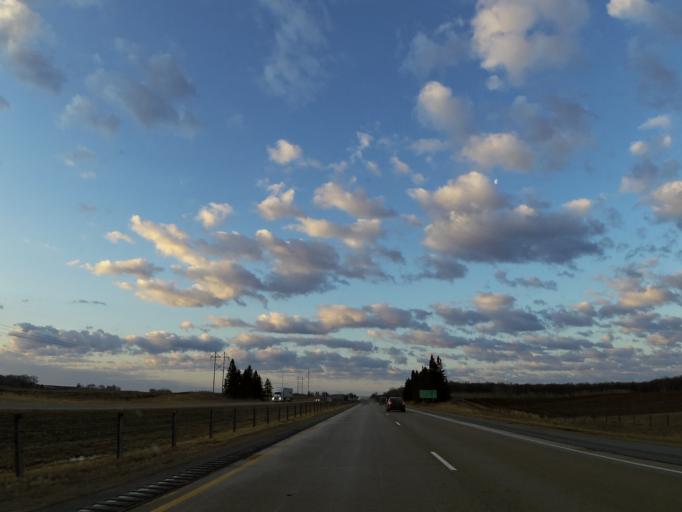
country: US
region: Minnesota
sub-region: Rice County
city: Dundas
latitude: 44.4166
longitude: -93.2929
